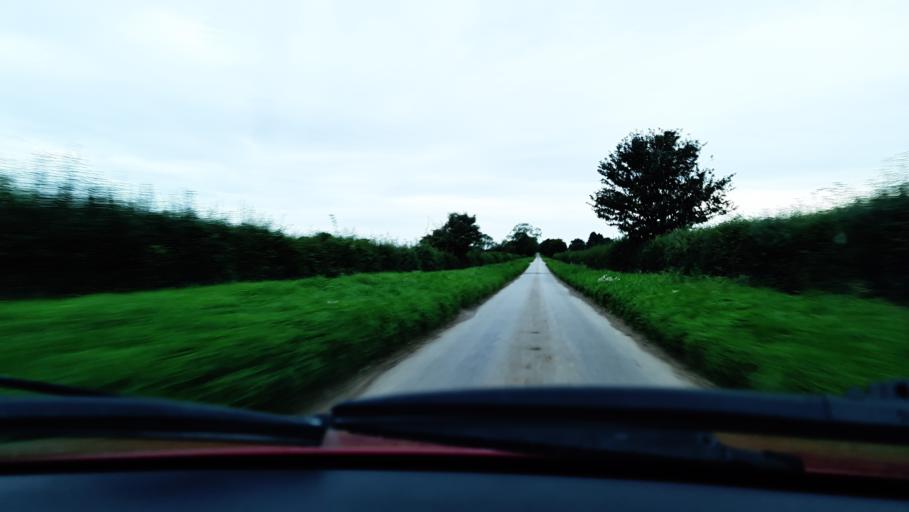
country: GB
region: England
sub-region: Oxfordshire
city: Somerton
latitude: 51.9587
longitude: -1.2483
